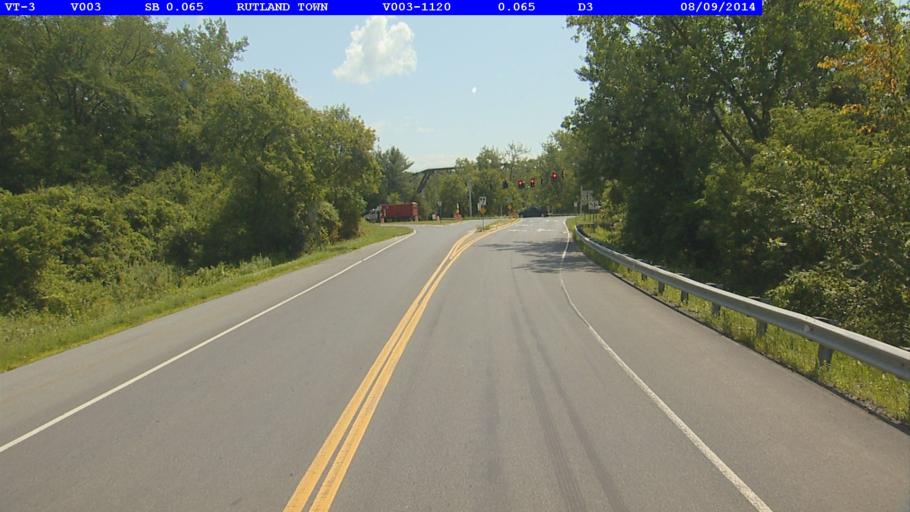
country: US
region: Vermont
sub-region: Rutland County
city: West Rutland
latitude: 43.6051
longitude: -73.0144
